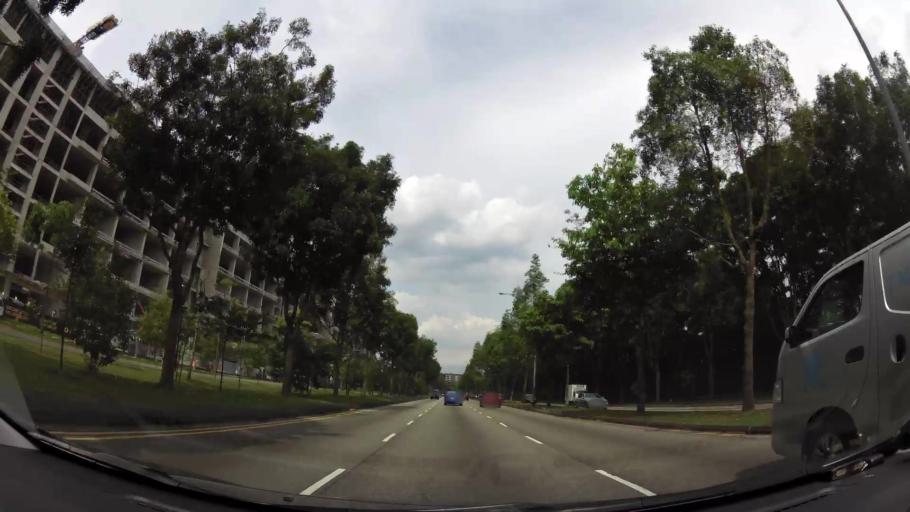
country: MY
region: Johor
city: Johor Bahru
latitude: 1.4368
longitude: 103.8073
